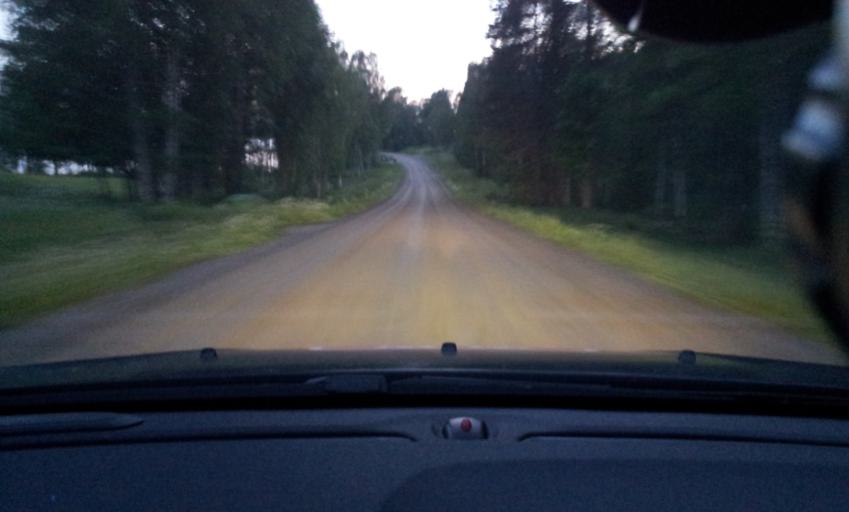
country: SE
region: Jaemtland
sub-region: Braecke Kommun
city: Braecke
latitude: 62.7167
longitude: 15.6051
